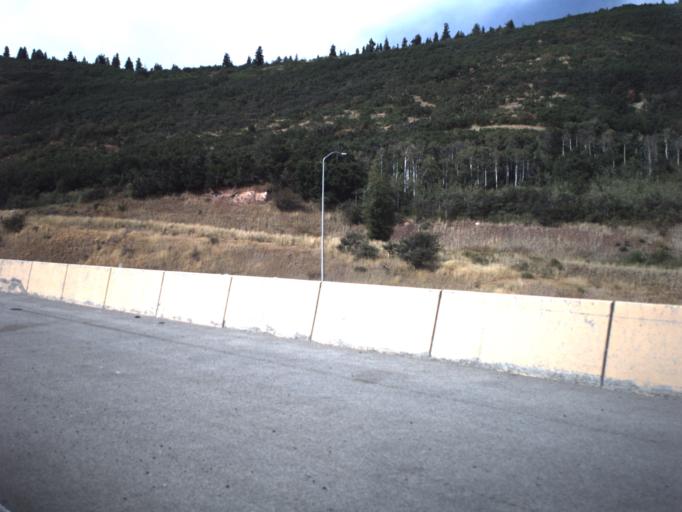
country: US
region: Utah
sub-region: Summit County
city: Summit Park
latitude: 40.7529
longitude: -111.6143
